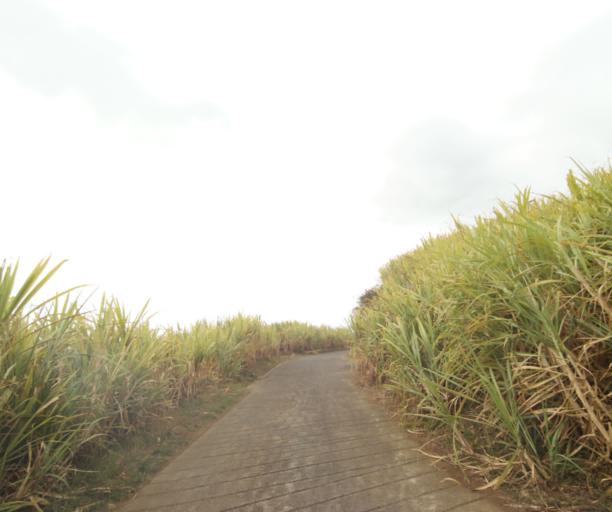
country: RE
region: Reunion
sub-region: Reunion
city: Saint-Paul
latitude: -21.0249
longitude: 55.3222
